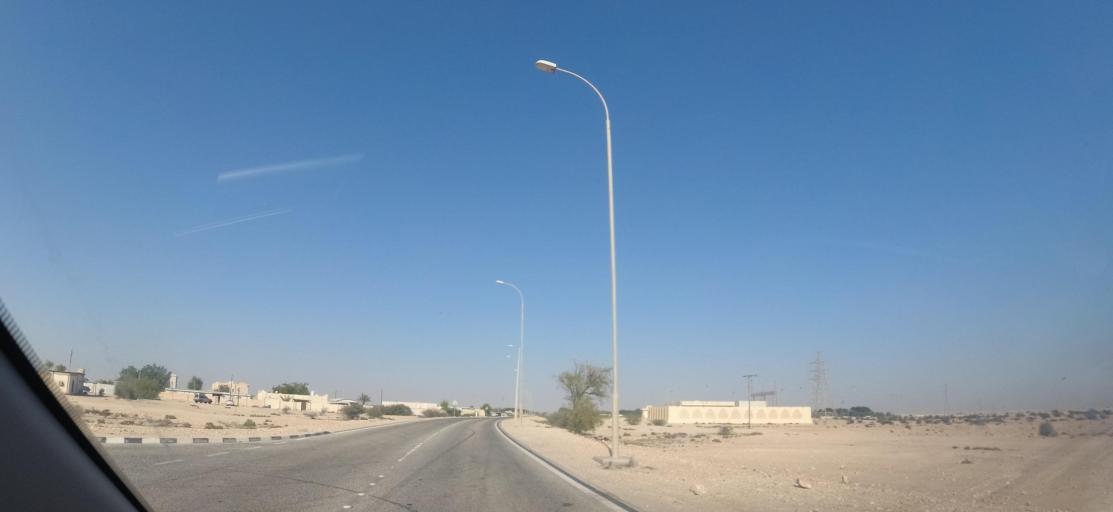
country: QA
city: Al Jumayliyah
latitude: 25.6193
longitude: 51.0857
